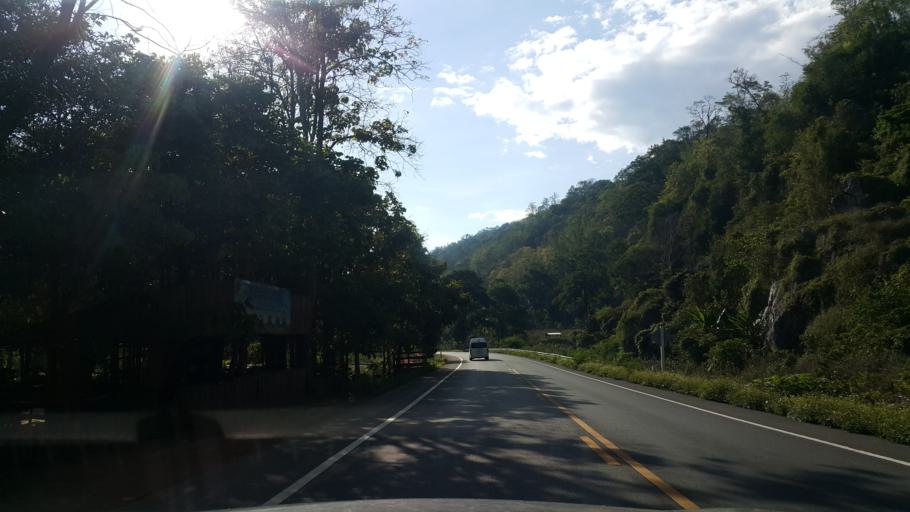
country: TH
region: Lampang
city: Wang Nuea
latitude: 19.0628
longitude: 99.7501
